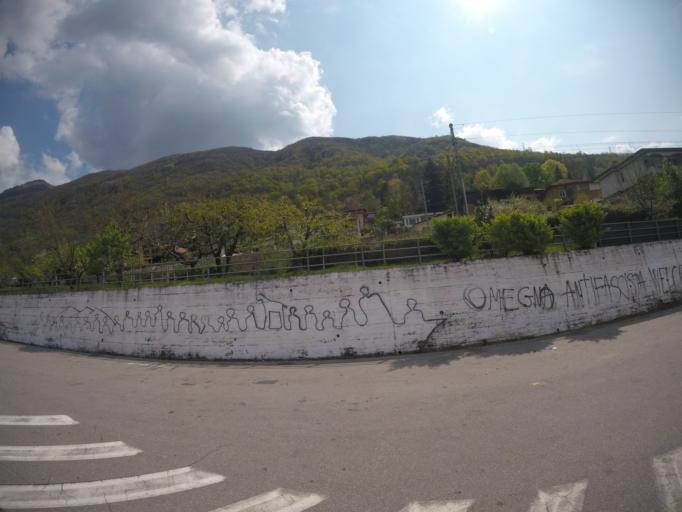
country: IT
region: Piedmont
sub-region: Provincia Verbano-Cusio-Ossola
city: Omegna
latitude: 45.8585
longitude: 8.4092
